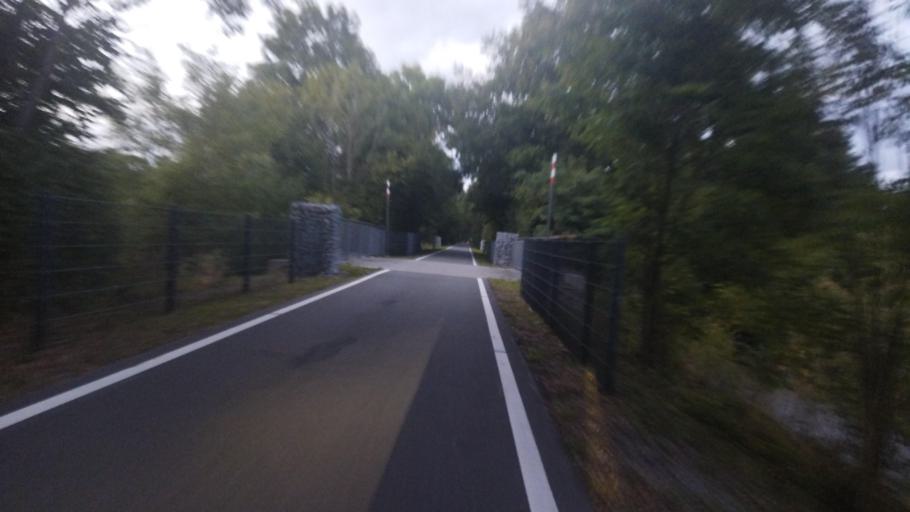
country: DE
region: North Rhine-Westphalia
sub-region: Regierungsbezirk Munster
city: Horstmar
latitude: 52.0975
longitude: 7.3301
